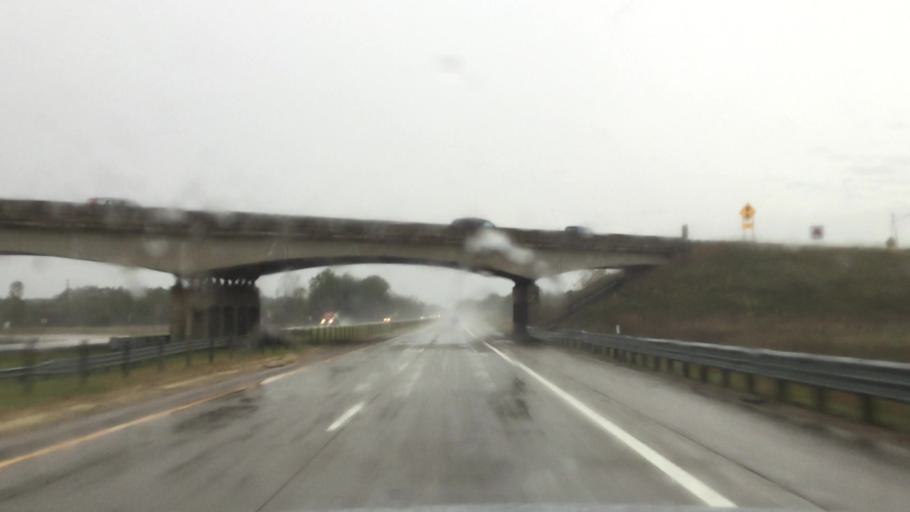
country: US
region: Michigan
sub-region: Van Buren County
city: Paw Paw
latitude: 42.2064
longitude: -85.8891
